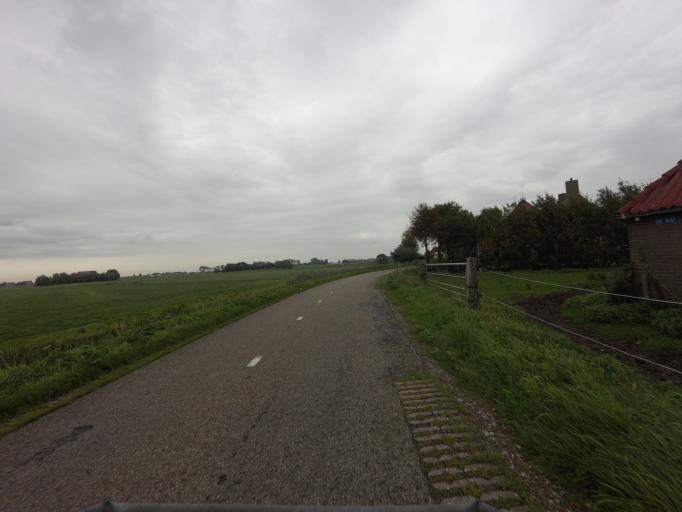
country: NL
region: Friesland
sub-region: Sudwest Fryslan
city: Bolsward
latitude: 53.0125
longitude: 5.5599
